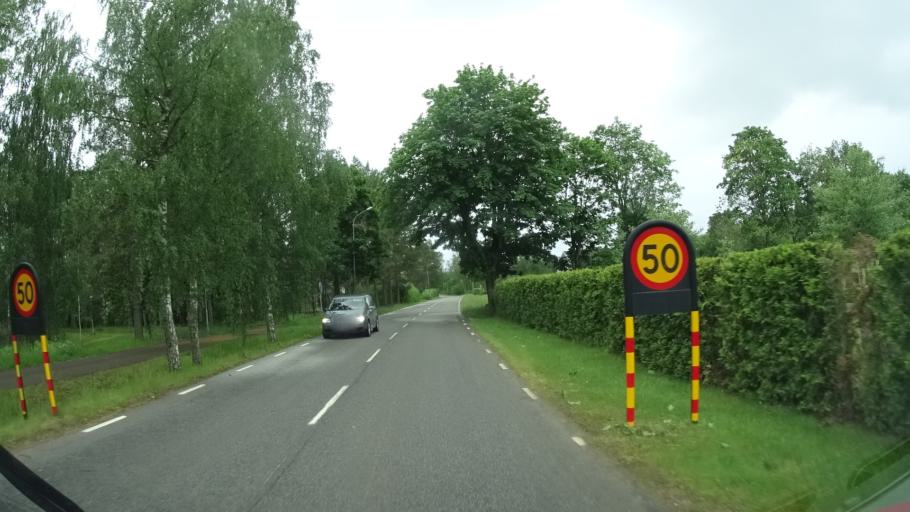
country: SE
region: Joenkoeping
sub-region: Eksjo Kommun
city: Mariannelund
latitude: 57.6757
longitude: 15.5929
